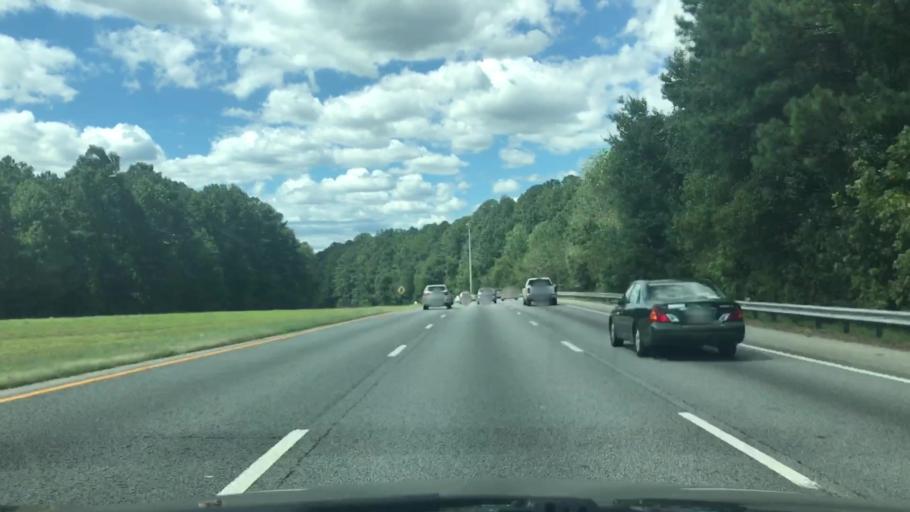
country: US
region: Georgia
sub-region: Gwinnett County
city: Mountain Park
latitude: 33.8235
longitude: -84.1314
